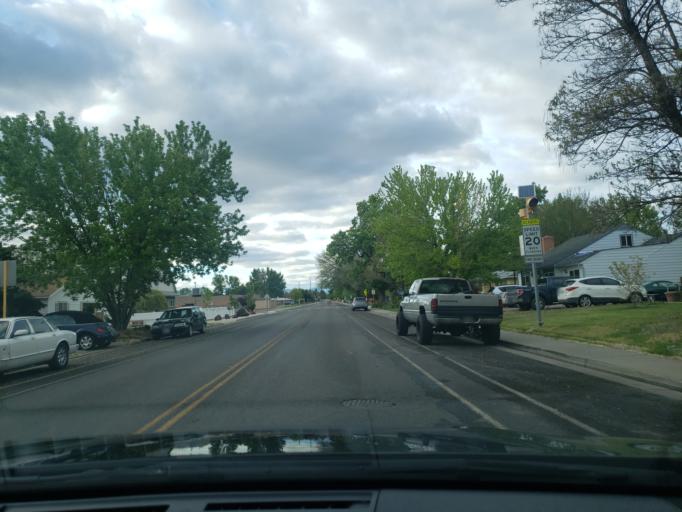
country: US
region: Colorado
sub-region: Mesa County
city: Fruita
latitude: 39.1617
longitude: -108.7336
